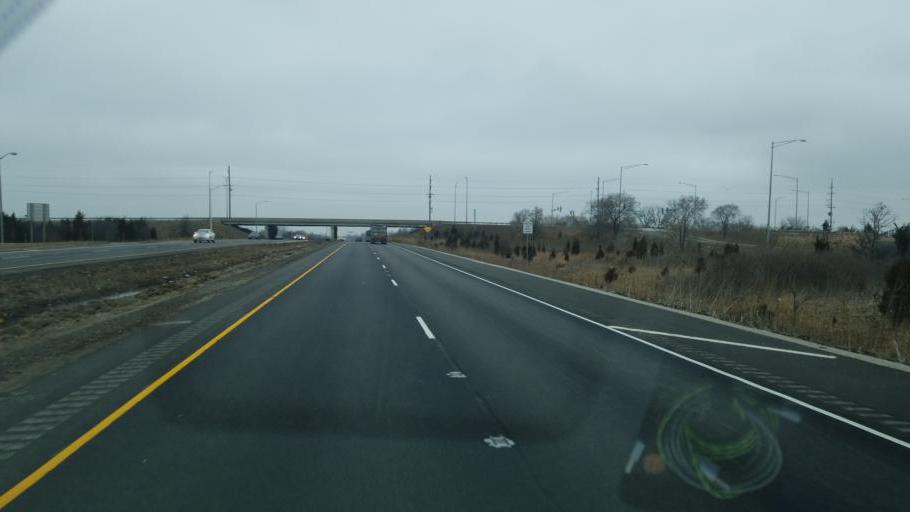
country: US
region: Illinois
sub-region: Lake County
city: Park City
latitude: 42.3576
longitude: -87.8947
